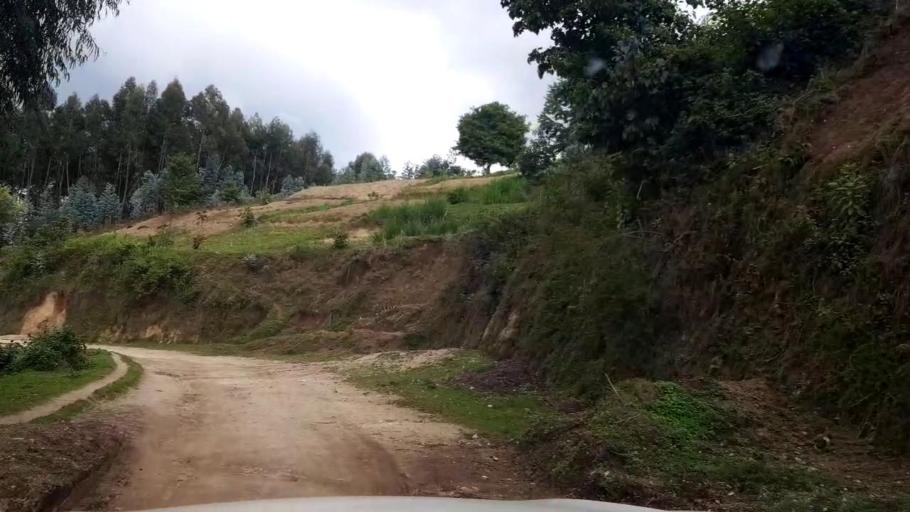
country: RW
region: Western Province
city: Kibuye
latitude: -1.8658
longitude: 29.5494
